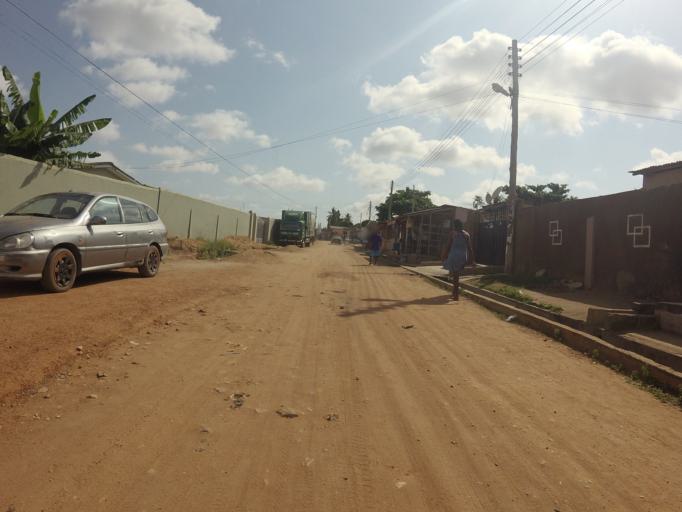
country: GH
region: Greater Accra
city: Dome
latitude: 5.6175
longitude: -0.2423
